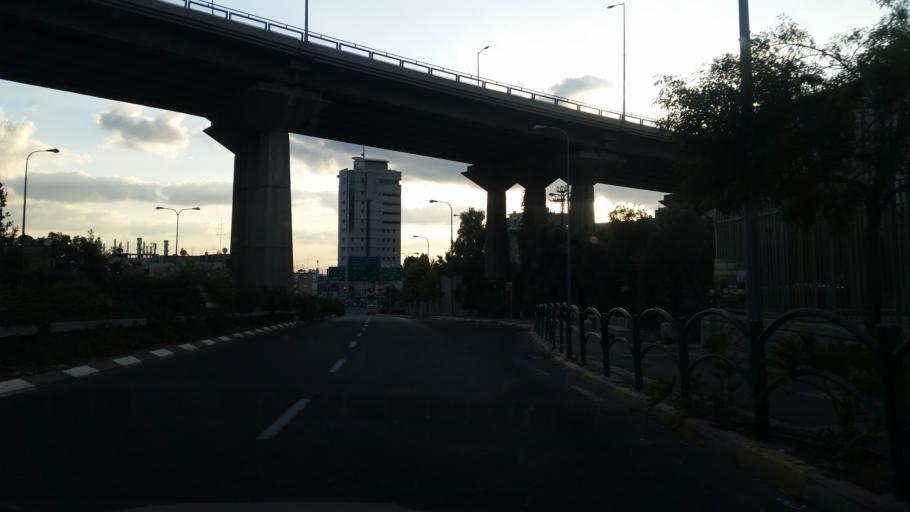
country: IL
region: Haifa
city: Haifa
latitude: 32.8038
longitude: 35.0075
